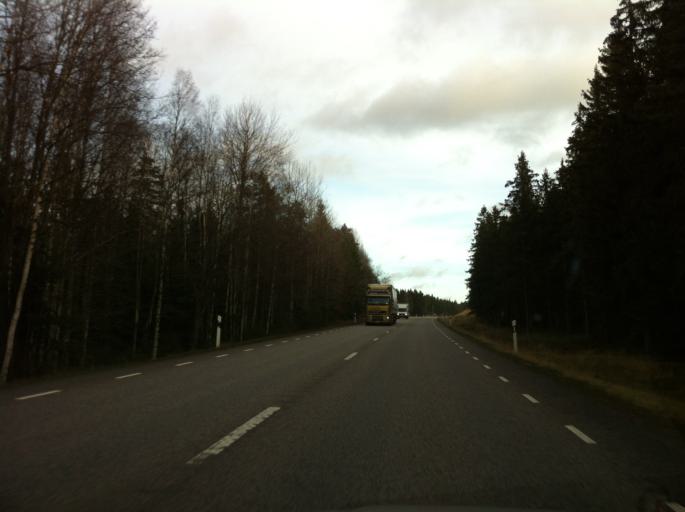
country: SE
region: Kronoberg
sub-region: Uppvidinge Kommun
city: Aseda
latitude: 57.1416
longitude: 15.2885
